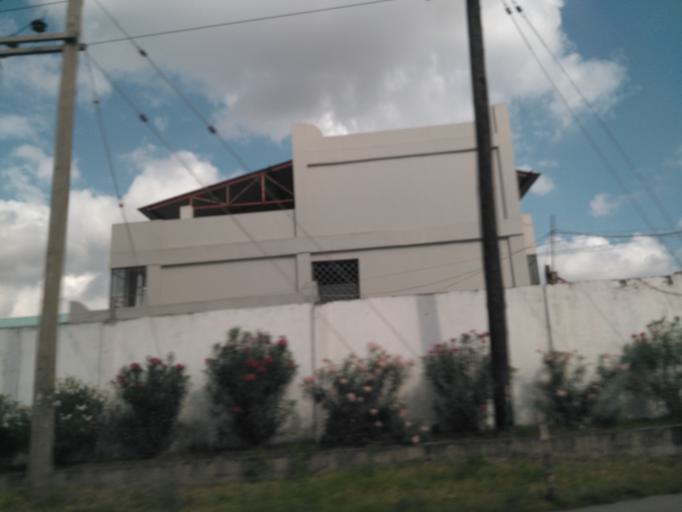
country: TZ
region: Dar es Salaam
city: Magomeni
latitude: -6.7627
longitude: 39.2369
